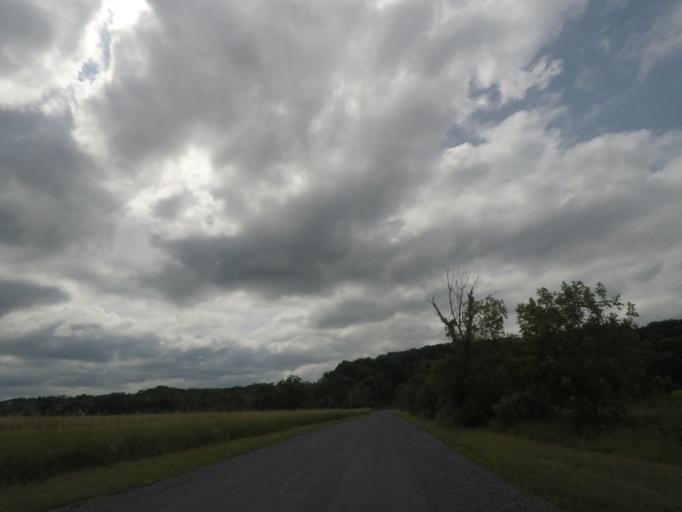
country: US
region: New York
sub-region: Saratoga County
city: Stillwater
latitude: 42.9850
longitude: -73.6171
